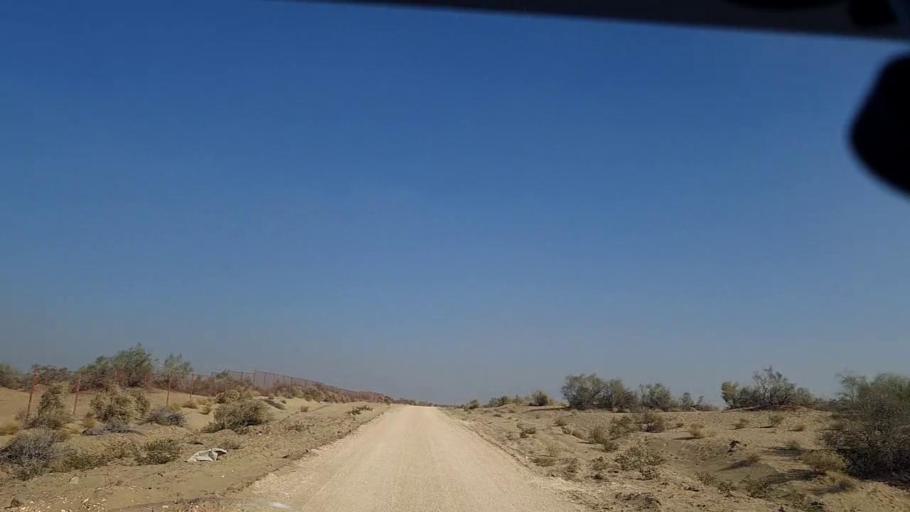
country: PK
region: Sindh
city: Khanpur
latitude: 27.5578
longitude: 69.3940
